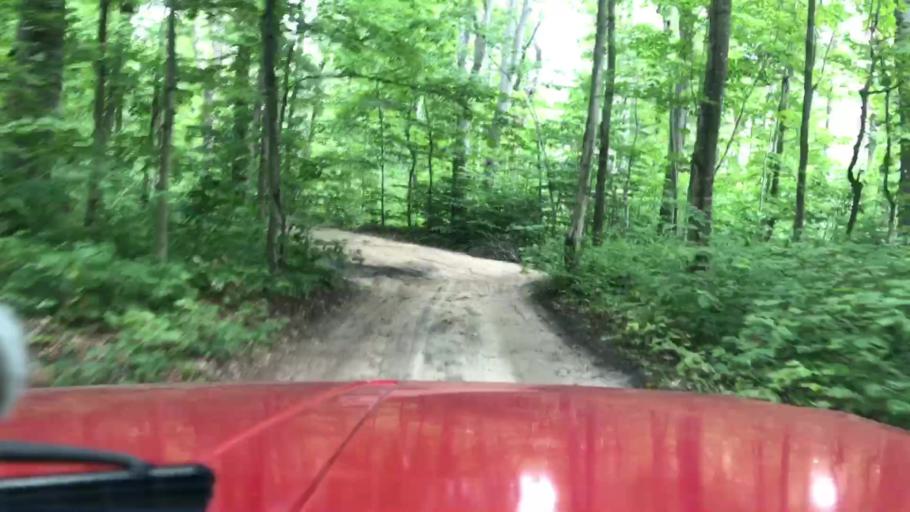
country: US
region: Michigan
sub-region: Charlevoix County
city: Charlevoix
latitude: 45.7245
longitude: -85.5639
